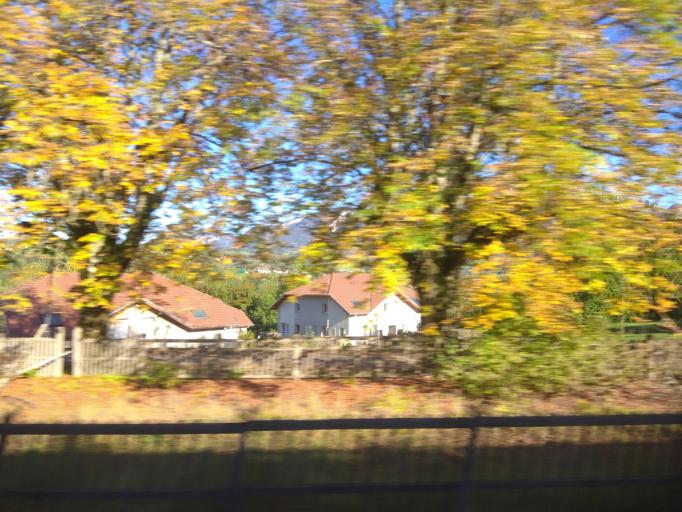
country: FR
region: Rhone-Alpes
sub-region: Departement de la Haute-Savoie
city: Saint-Martin-Bellevue
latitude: 45.9673
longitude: 6.1576
